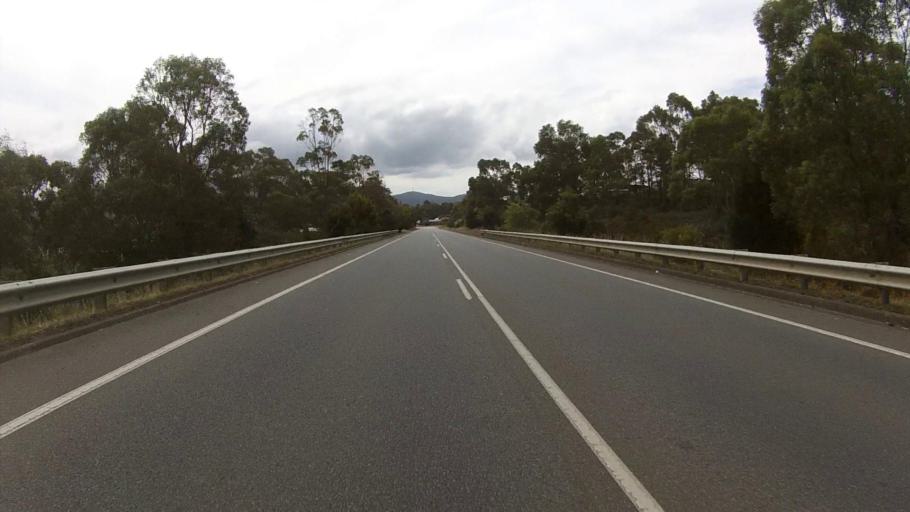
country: AU
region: Tasmania
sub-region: Kingborough
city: Kingston
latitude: -42.9932
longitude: 147.2946
